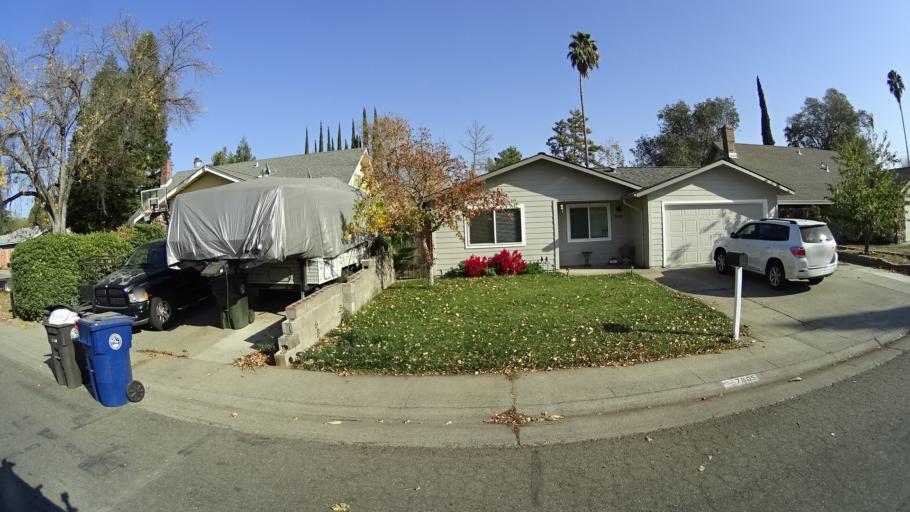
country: US
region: California
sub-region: Sacramento County
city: Citrus Heights
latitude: 38.6869
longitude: -121.2764
